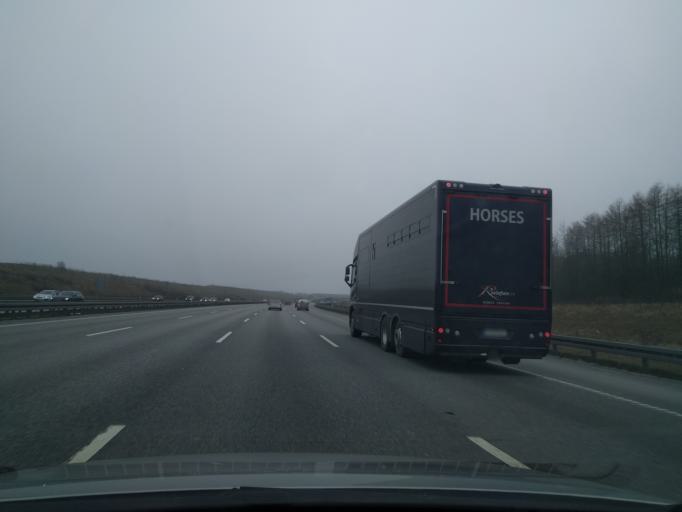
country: DK
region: Zealand
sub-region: Solrod Kommune
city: Solrod Strand
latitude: 55.5563
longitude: 12.2296
